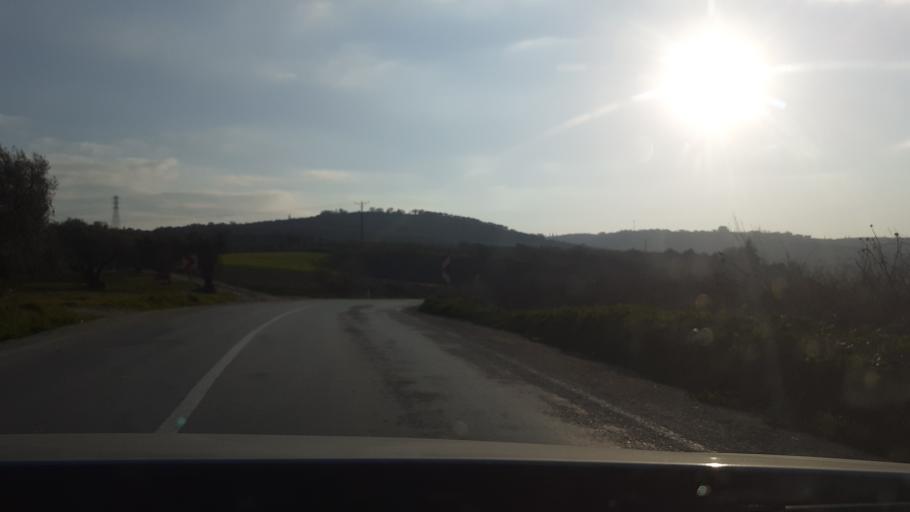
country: TR
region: Hatay
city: Oymakli
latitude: 36.1118
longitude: 36.2788
